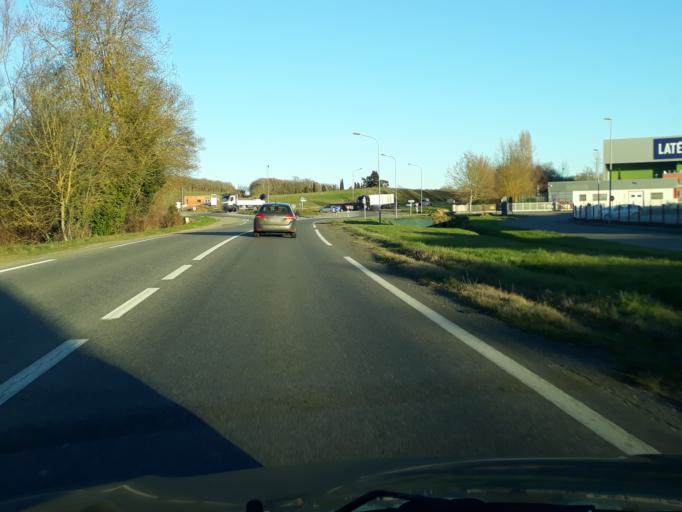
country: FR
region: Midi-Pyrenees
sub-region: Departement du Gers
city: Gimont
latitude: 43.6240
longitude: 0.9041
